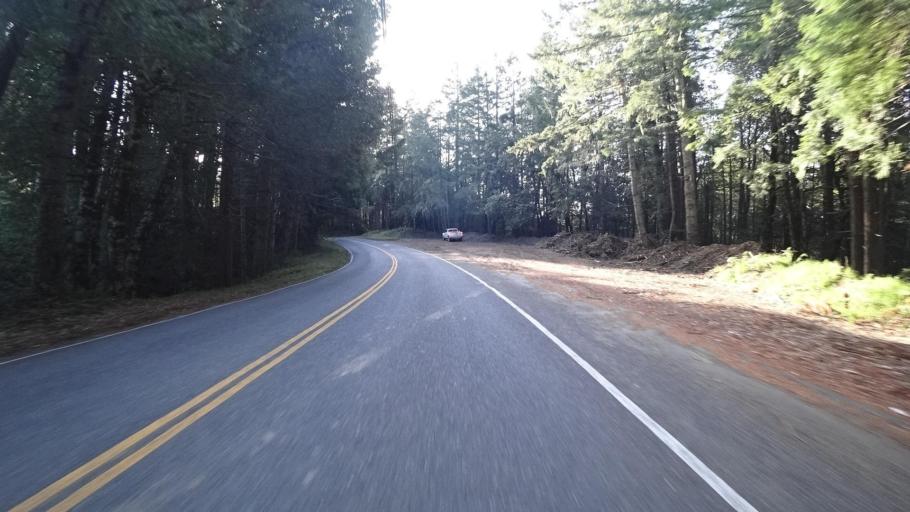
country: US
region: California
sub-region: Humboldt County
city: Bayside
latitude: 40.7484
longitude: -123.9749
